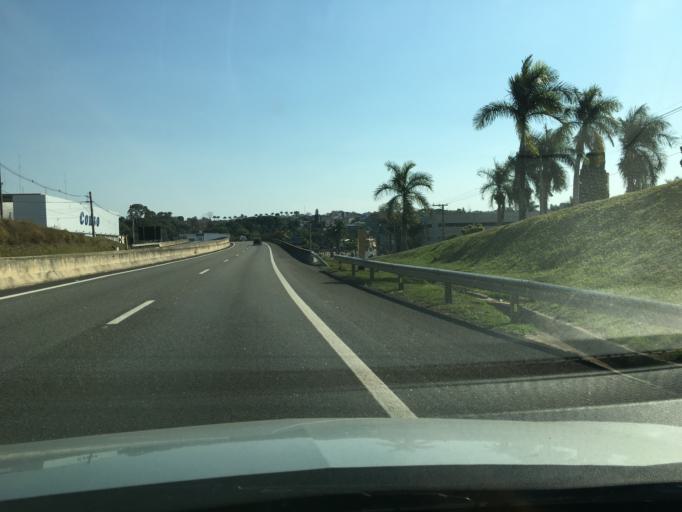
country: BR
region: Sao Paulo
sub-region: Sao Joao Da Boa Vista
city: Sao Joao da Boa Vista
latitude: -21.9792
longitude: -46.7831
